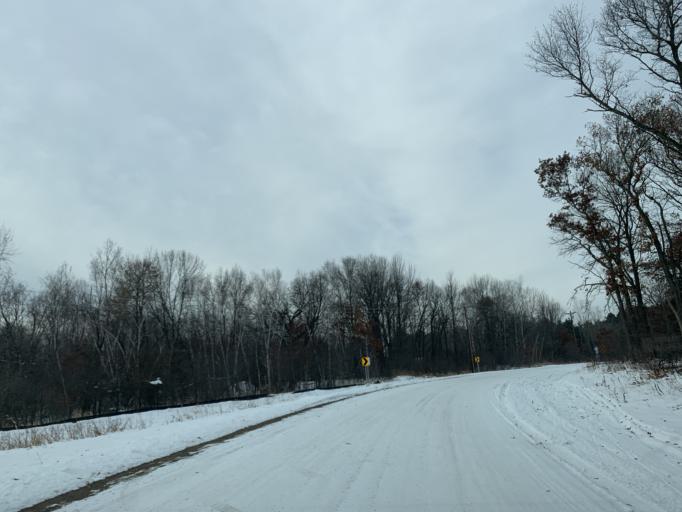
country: US
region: Minnesota
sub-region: Washington County
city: Forest Lake
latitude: 45.2904
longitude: -93.0060
